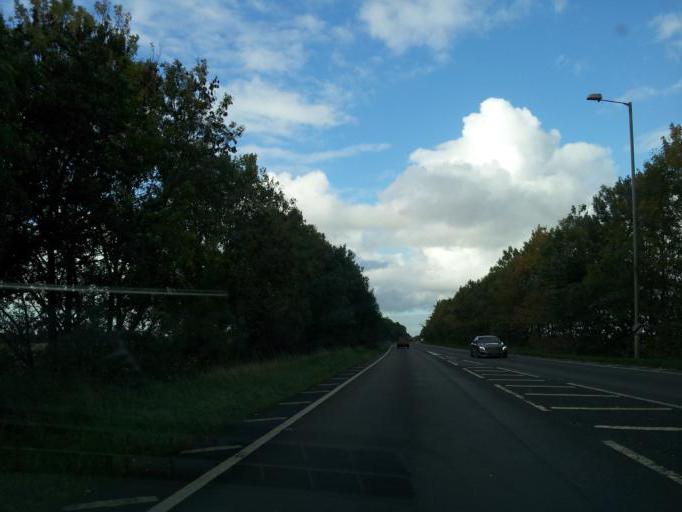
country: GB
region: England
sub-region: Norfolk
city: Terrington St Clement
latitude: 52.7465
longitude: 0.2922
